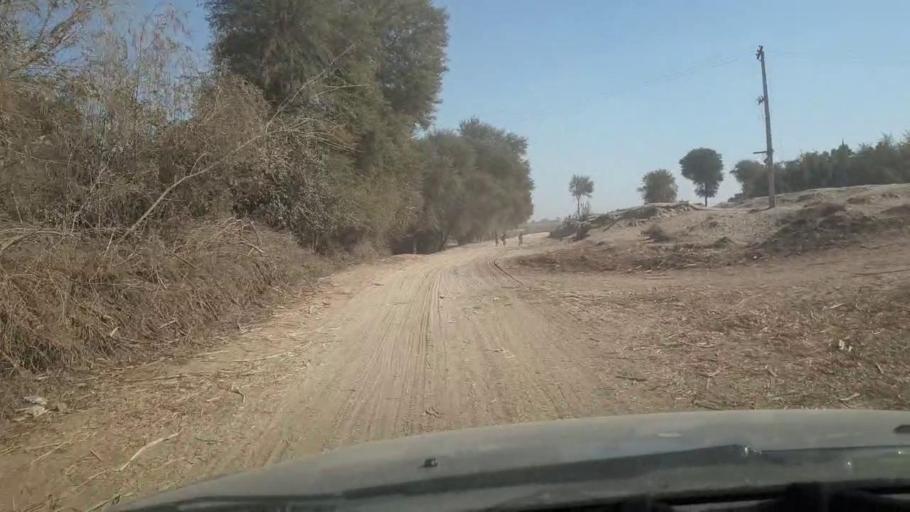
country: PK
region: Sindh
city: Ghotki
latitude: 28.0156
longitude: 69.2291
